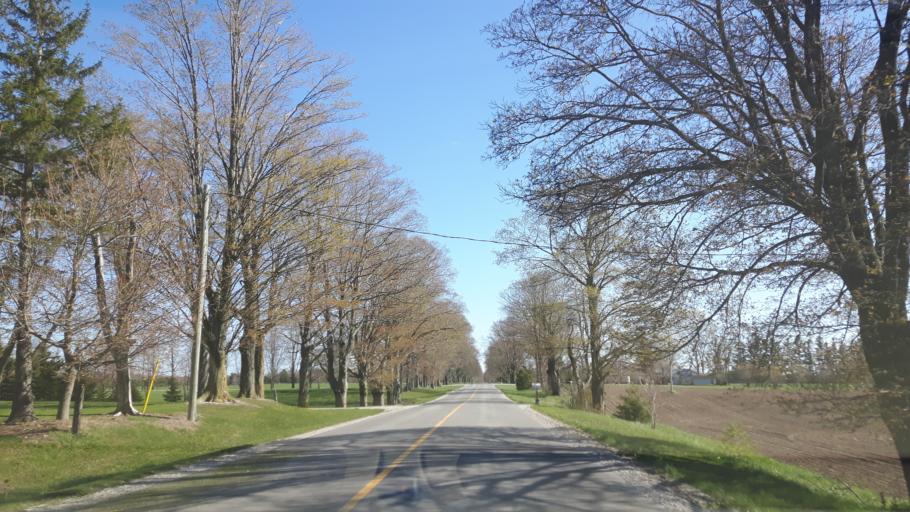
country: CA
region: Ontario
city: Goderich
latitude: 43.6260
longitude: -81.6644
